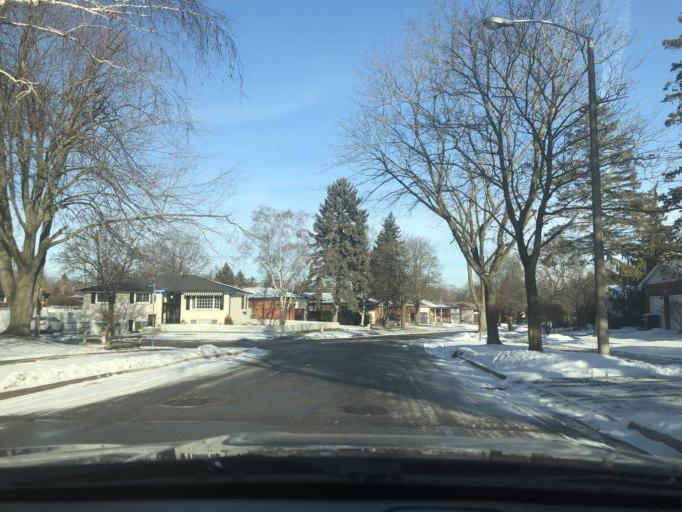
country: CA
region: Ontario
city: Scarborough
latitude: 43.7732
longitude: -79.1506
